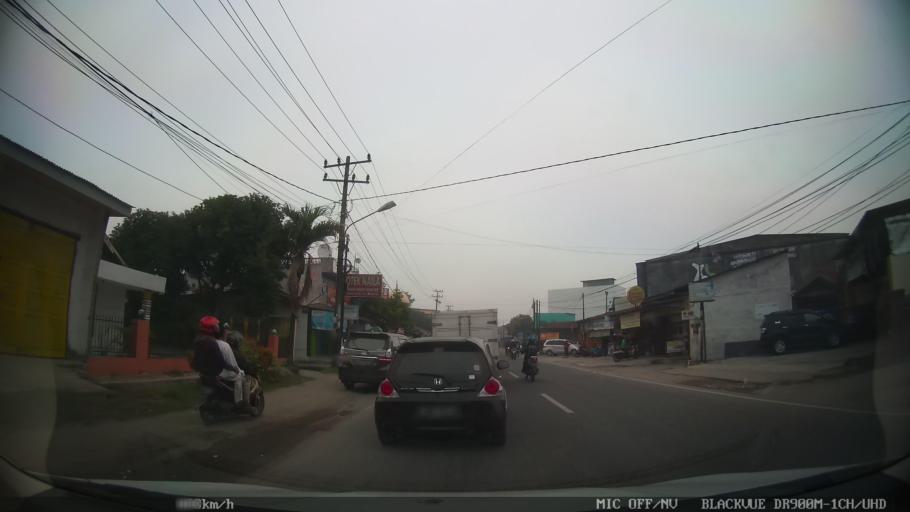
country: ID
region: North Sumatra
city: Deli Tua
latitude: 3.5469
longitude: 98.7175
